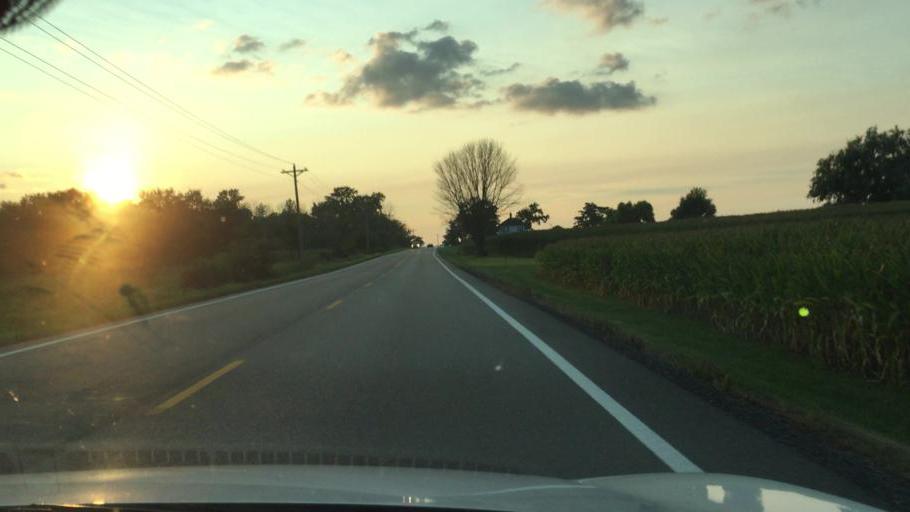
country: US
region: Ohio
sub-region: Champaign County
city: Mechanicsburg
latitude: 40.0469
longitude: -83.5176
